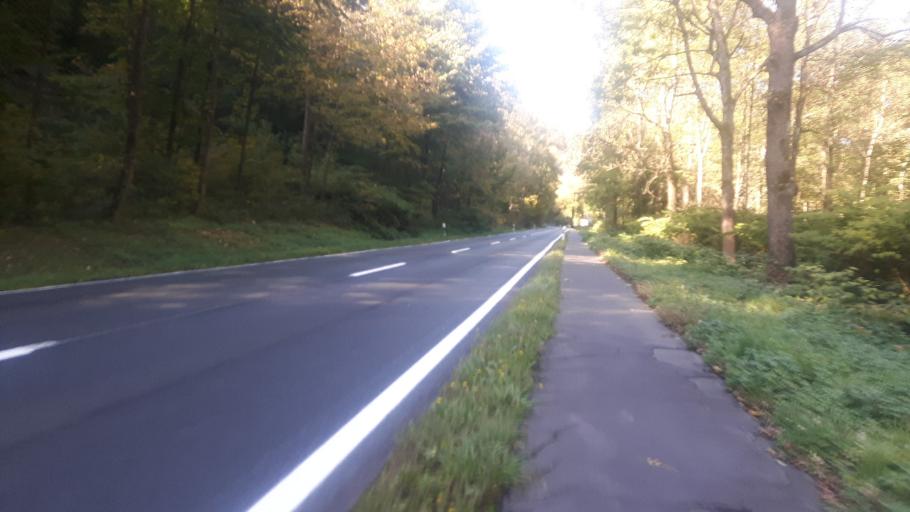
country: DE
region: Rheinland-Pfalz
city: Wissen
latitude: 50.7832
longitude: 7.7544
